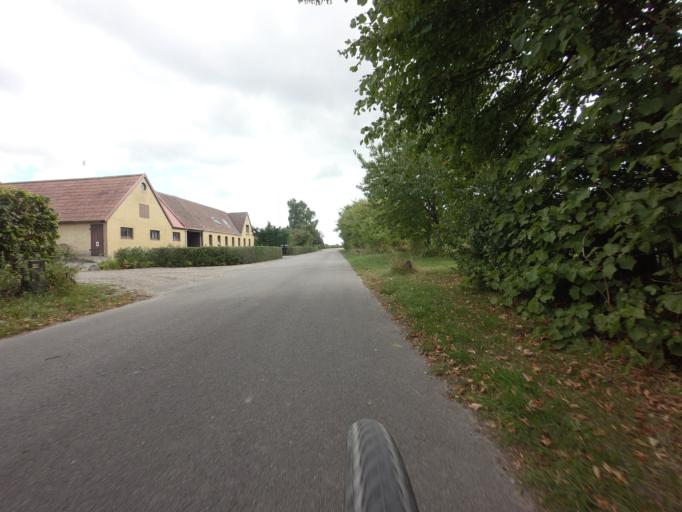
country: DK
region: Zealand
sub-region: Vordingborg Kommune
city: Stege
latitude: 55.0117
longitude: 12.3263
